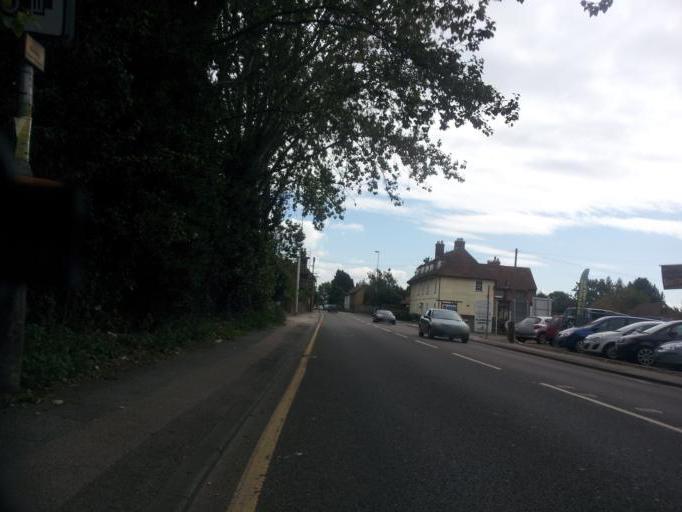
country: GB
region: England
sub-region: Kent
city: Rainham
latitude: 51.3604
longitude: 0.6233
